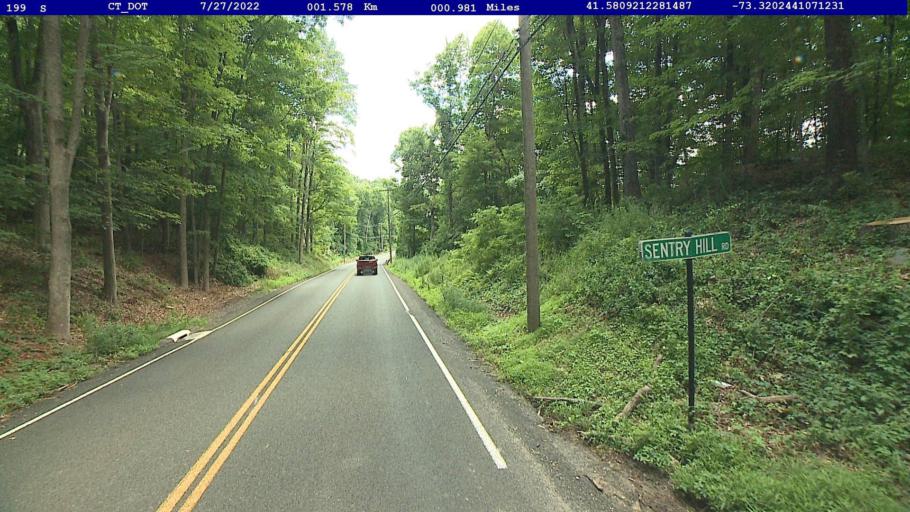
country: US
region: Connecticut
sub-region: Litchfield County
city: New Milford
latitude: 41.5809
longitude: -73.3202
